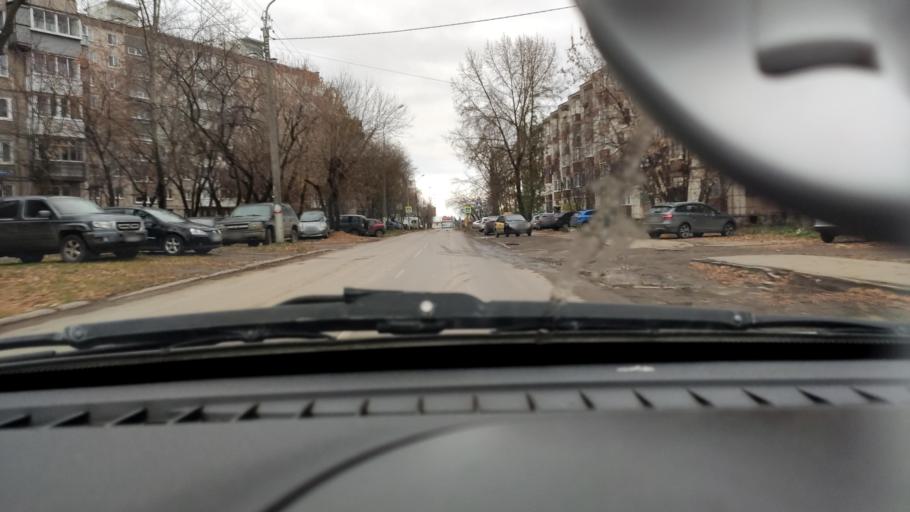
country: RU
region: Perm
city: Kondratovo
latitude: 57.9633
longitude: 56.1690
